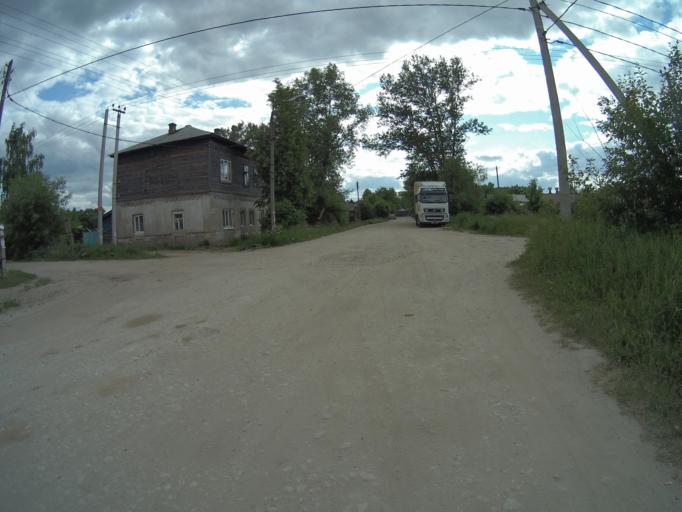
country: RU
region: Vladimir
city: Sudogda
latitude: 55.9492
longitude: 40.8609
